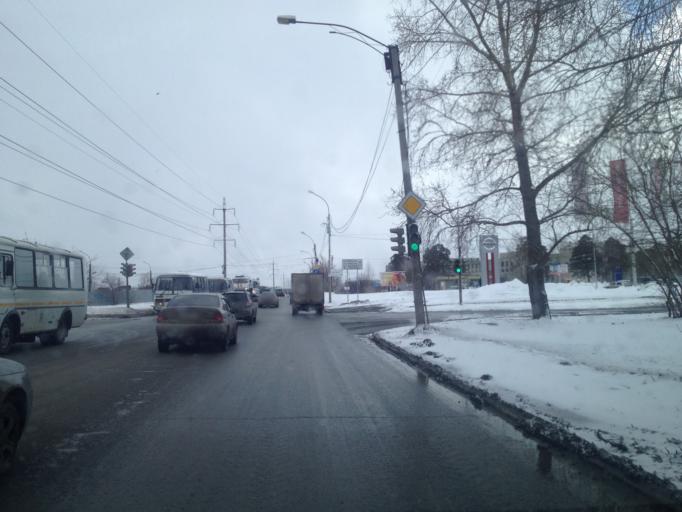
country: RU
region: Sverdlovsk
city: Sovkhoznyy
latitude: 56.7659
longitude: 60.5929
